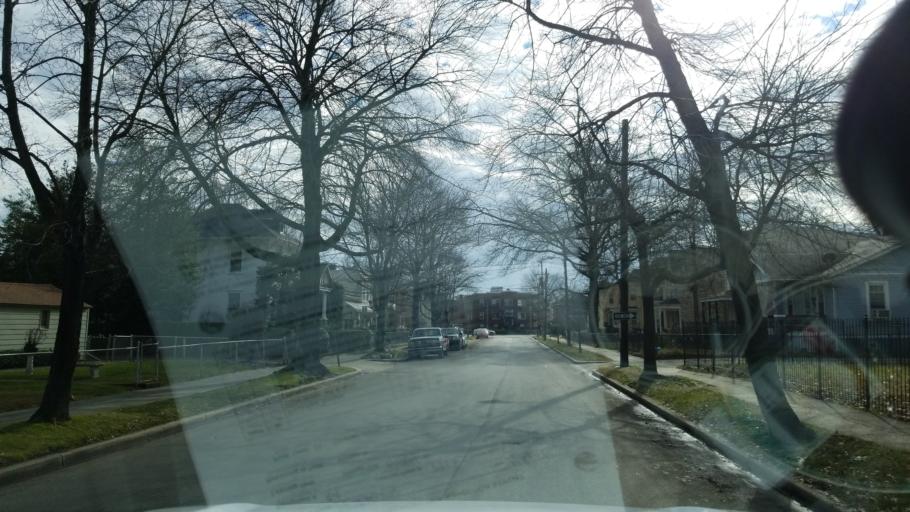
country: US
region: Maryland
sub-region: Prince George's County
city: Glassmanor
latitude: 38.8450
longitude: -76.9947
